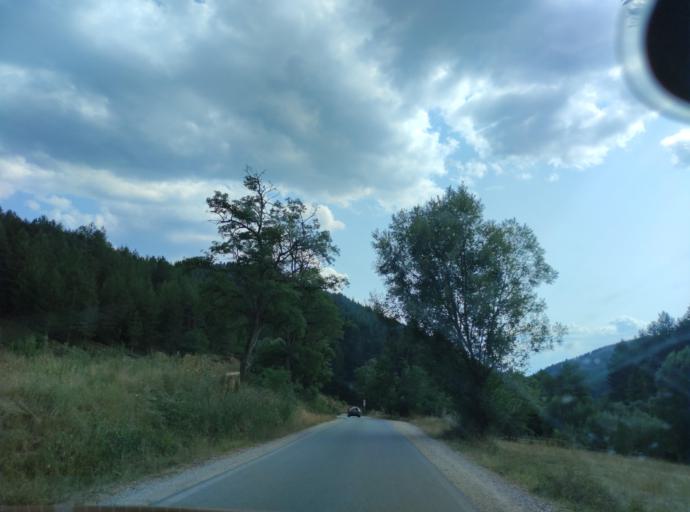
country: BG
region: Blagoevgrad
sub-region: Obshtina Belitsa
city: Belitsa
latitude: 41.9703
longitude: 23.5560
